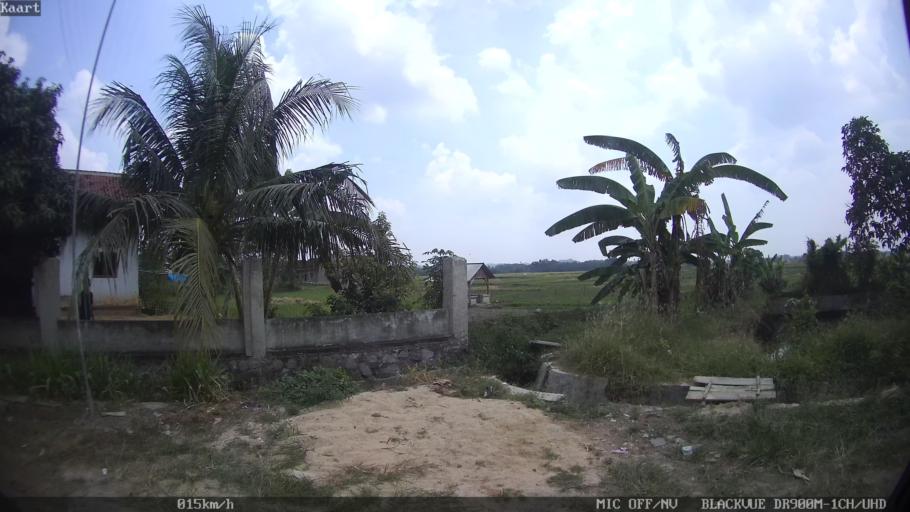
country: ID
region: Lampung
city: Pringsewu
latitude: -5.3470
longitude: 104.9897
